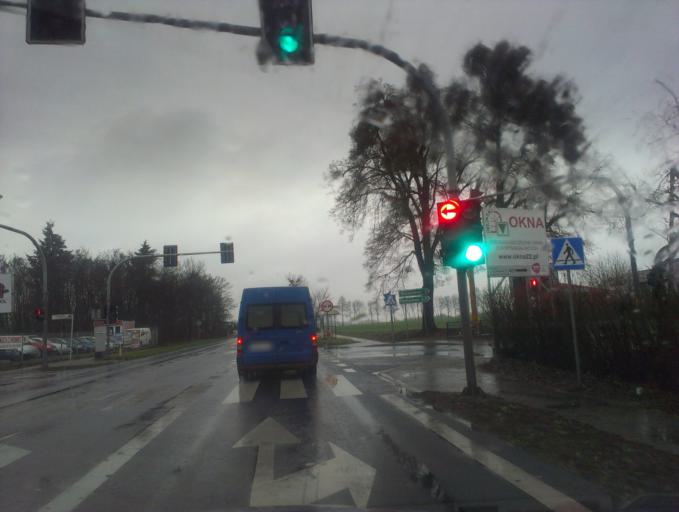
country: PL
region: Greater Poland Voivodeship
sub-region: Powiat obornicki
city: Oborniki
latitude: 52.6792
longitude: 16.8689
